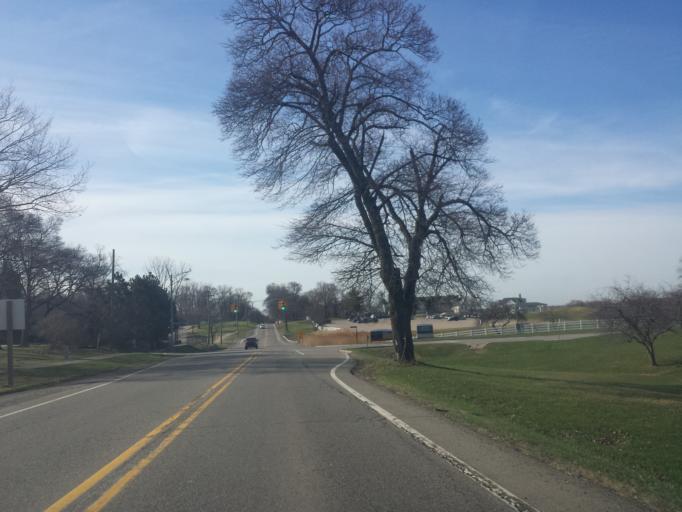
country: US
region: Michigan
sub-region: Oakland County
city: Auburn Hills
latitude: 42.6762
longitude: -83.1939
